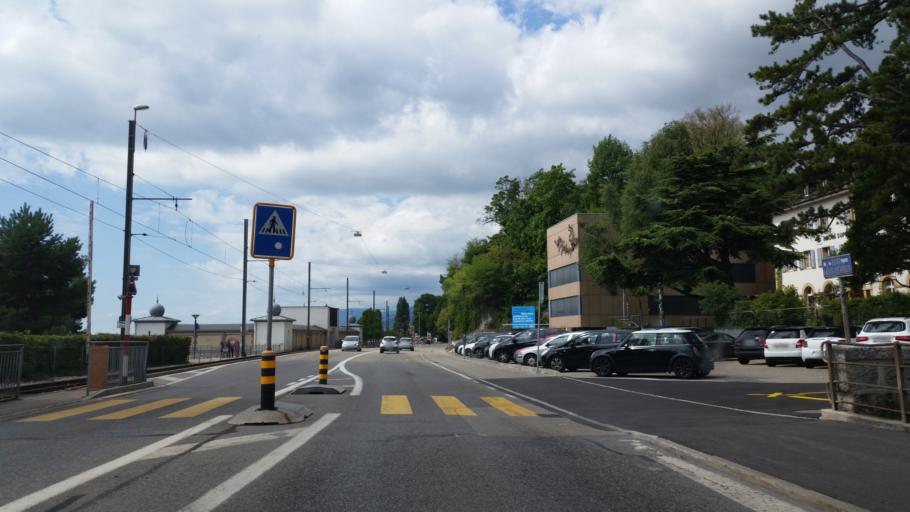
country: CH
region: Neuchatel
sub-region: Neuchatel District
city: Neuchatel
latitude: 46.9891
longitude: 6.9218
